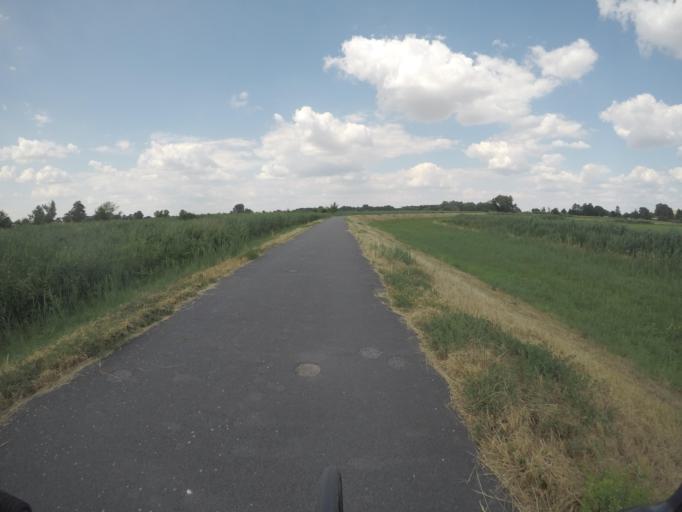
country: DE
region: Brandenburg
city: Roskow
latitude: 52.4546
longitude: 12.7651
